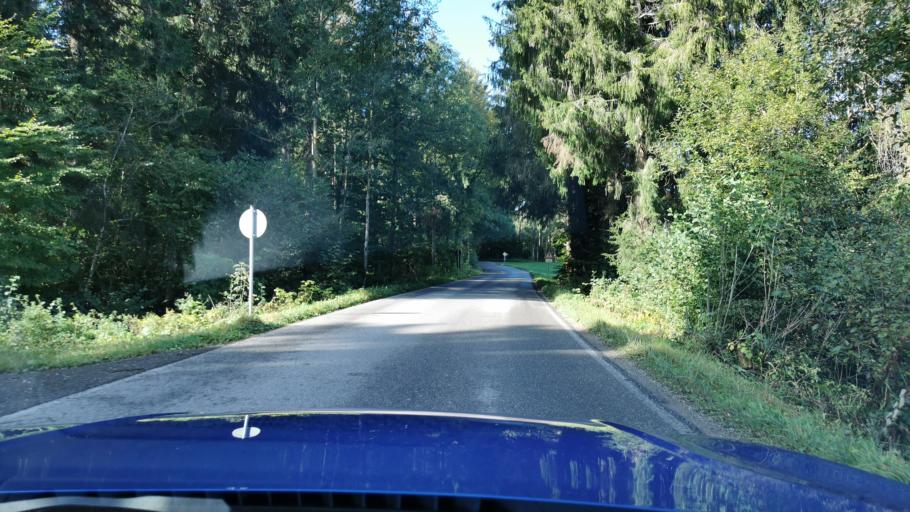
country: DE
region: Bavaria
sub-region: Upper Bavaria
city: Warngau
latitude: 47.8169
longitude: 11.7014
